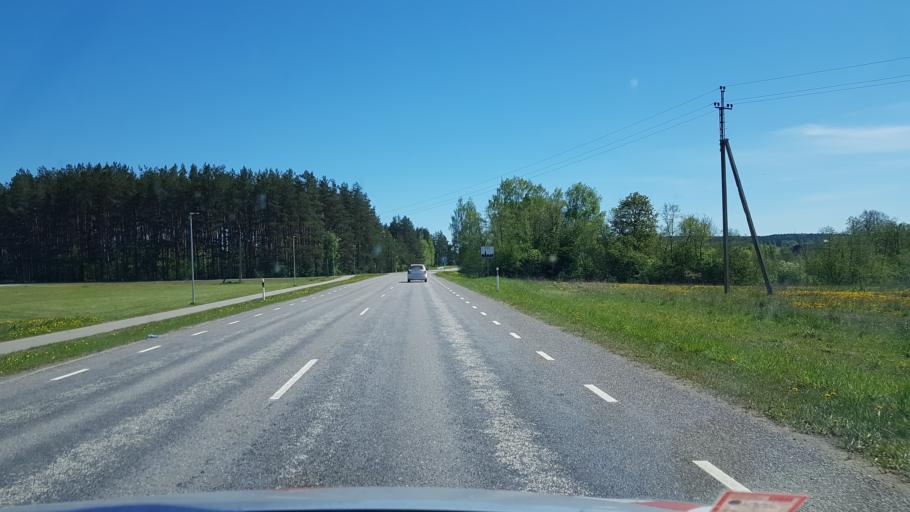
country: EE
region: Tartu
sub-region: UElenurme vald
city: Ulenurme
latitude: 58.3039
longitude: 26.8609
